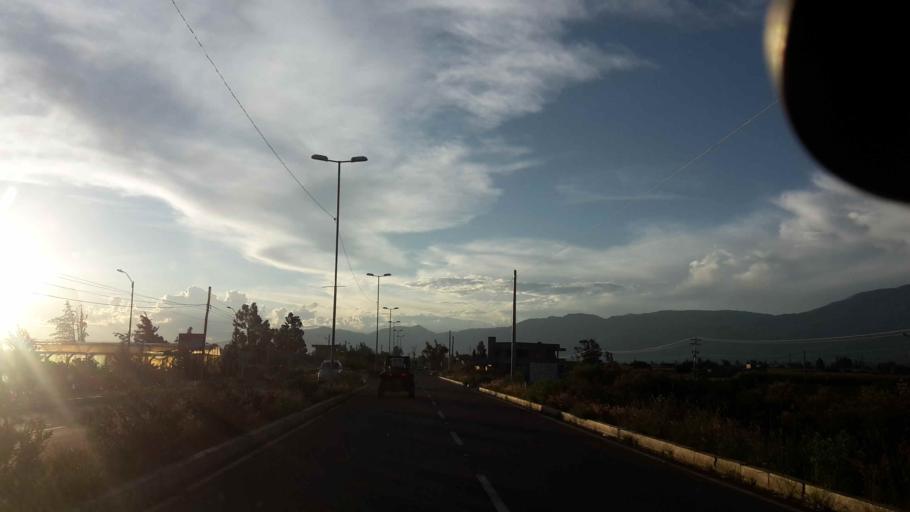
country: BO
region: Cochabamba
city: Arani
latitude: -17.5655
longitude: -65.7880
